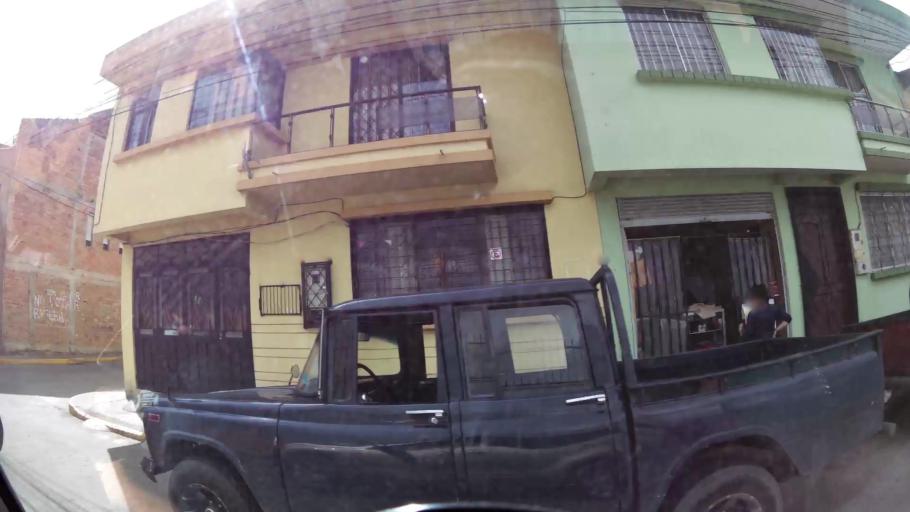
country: EC
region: Azuay
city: Cuenca
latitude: -2.8849
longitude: -78.9901
